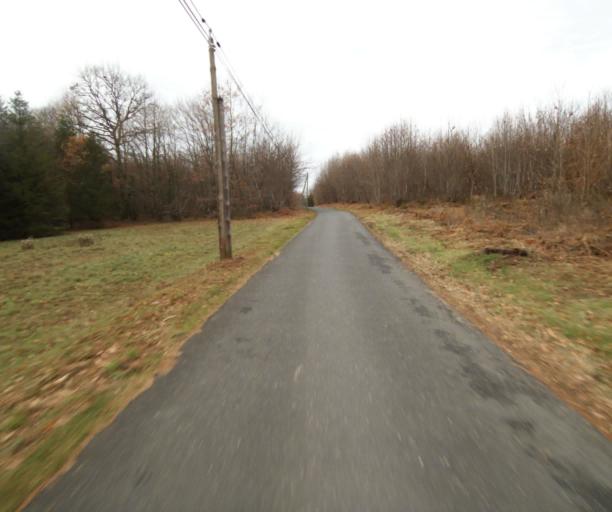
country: FR
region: Limousin
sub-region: Departement de la Correze
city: Chameyrat
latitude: 45.2372
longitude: 1.6754
